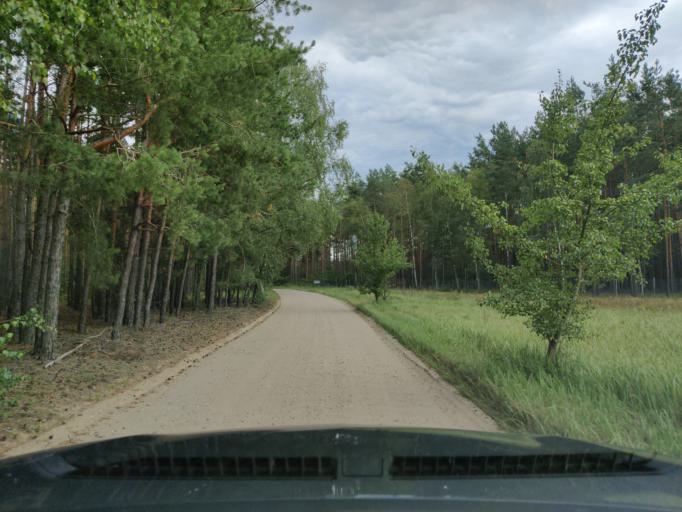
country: PL
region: Masovian Voivodeship
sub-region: Powiat pultuski
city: Pultusk
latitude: 52.7617
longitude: 21.1338
